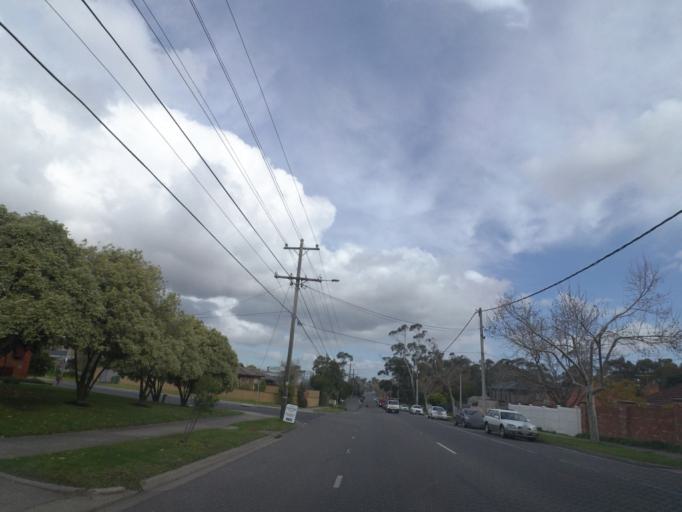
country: AU
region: Victoria
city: Mitcham
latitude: -37.8274
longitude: 145.2134
